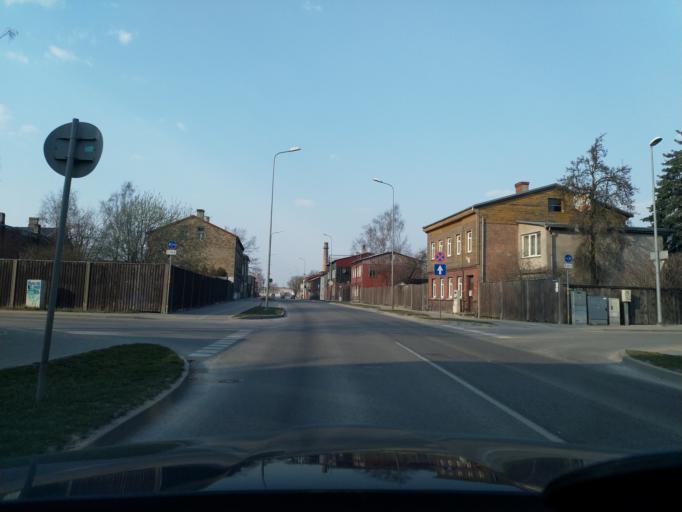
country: LV
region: Liepaja
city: Liepaja
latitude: 56.5066
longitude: 21.0250
